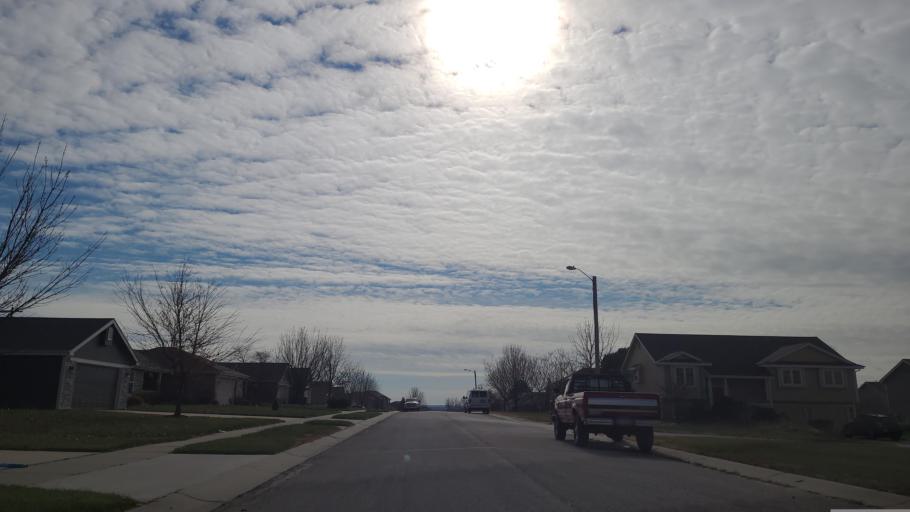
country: US
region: Kansas
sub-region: Douglas County
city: Eudora
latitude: 38.9187
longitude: -95.0986
